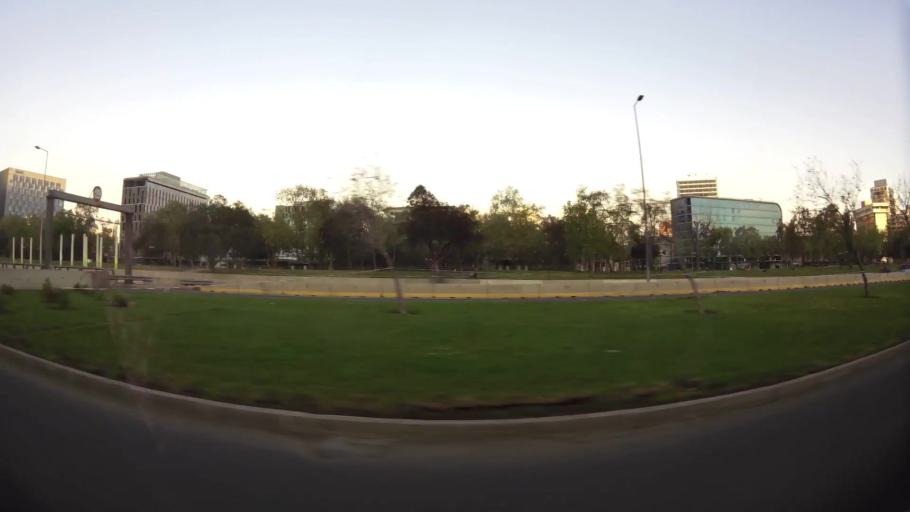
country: CL
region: Santiago Metropolitan
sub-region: Provincia de Santiago
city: Santiago
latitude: -33.4265
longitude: -70.6234
